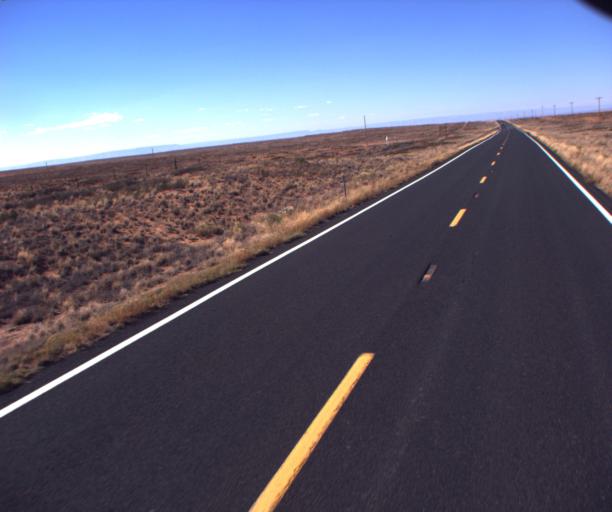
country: US
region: Arizona
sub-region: Coconino County
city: Tuba City
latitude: 36.0055
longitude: -111.0494
